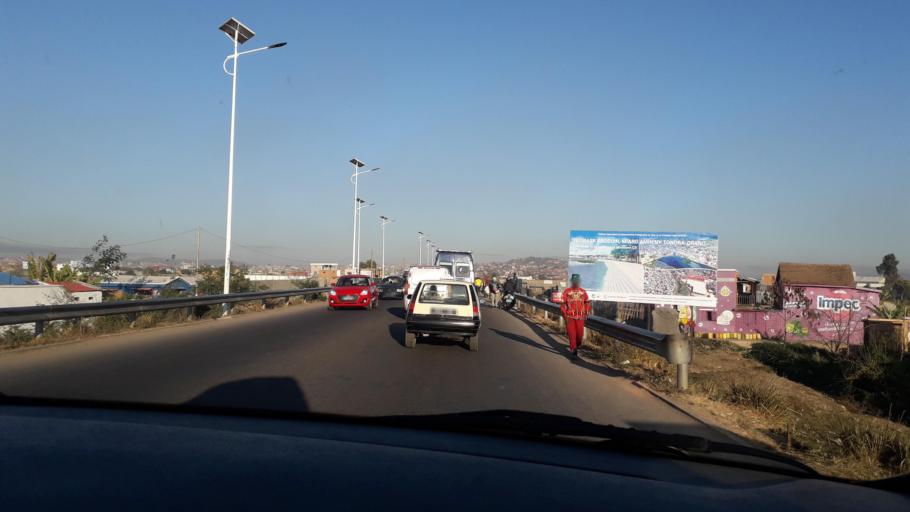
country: MG
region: Analamanga
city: Antananarivo
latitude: -18.8942
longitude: 47.5054
